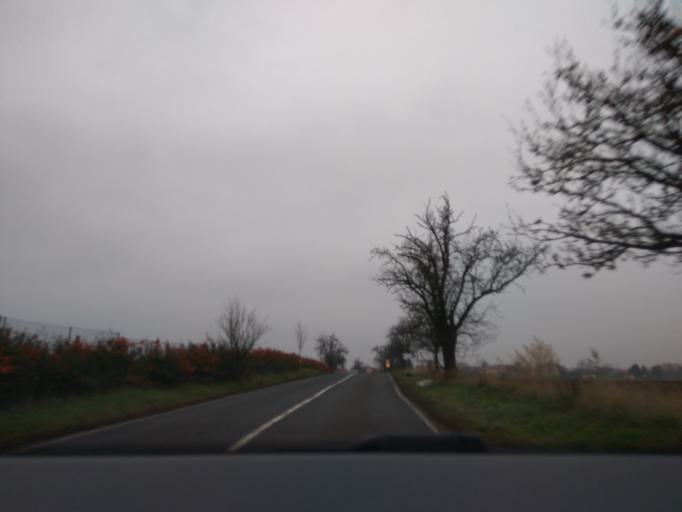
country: CZ
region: Praha
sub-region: Praha 19
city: Kbely
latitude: 50.1499
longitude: 14.5434
